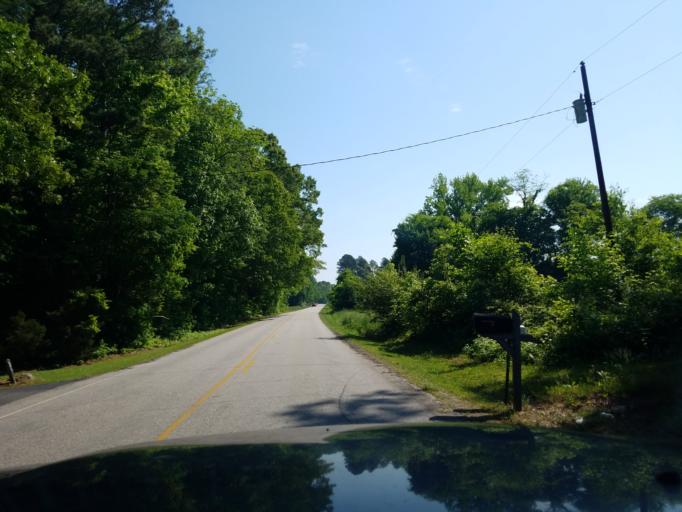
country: US
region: North Carolina
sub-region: Vance County
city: Henderson
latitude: 36.4032
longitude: -78.4154
